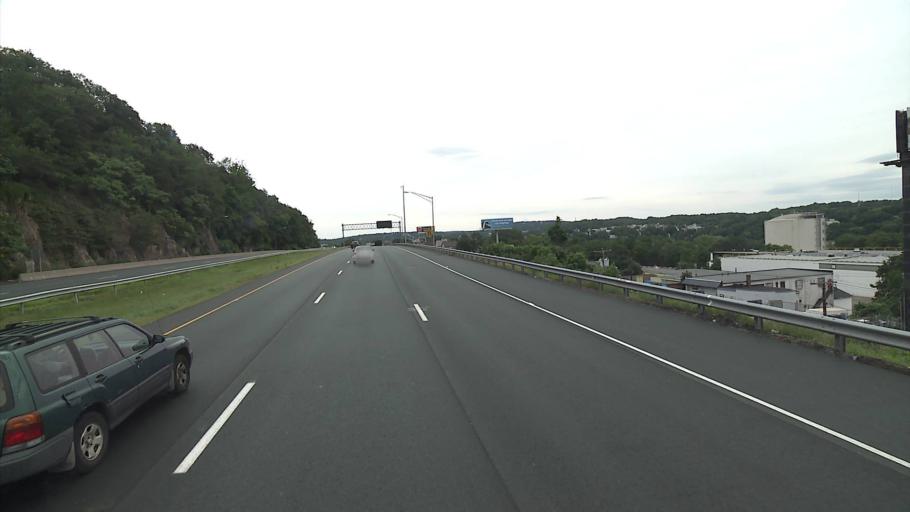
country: US
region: Connecticut
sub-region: New Haven County
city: Waterbury
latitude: 41.5314
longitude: -73.0441
